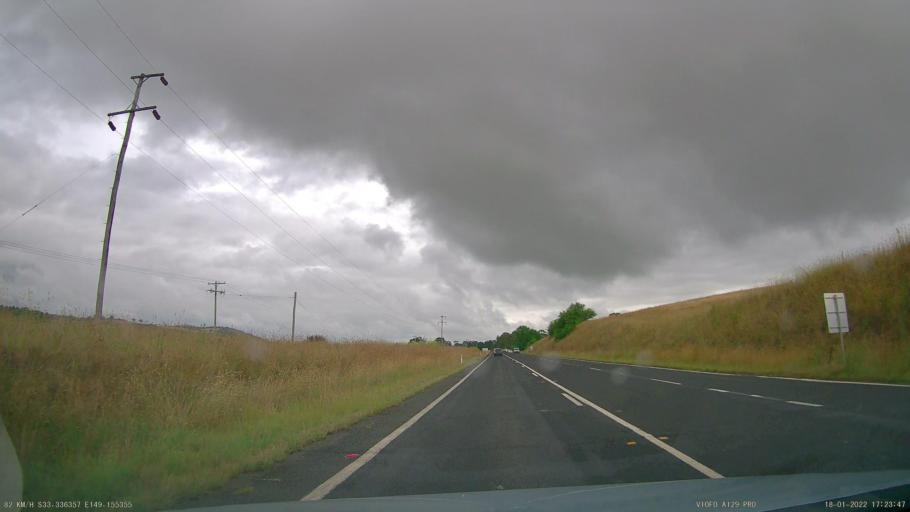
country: AU
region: New South Wales
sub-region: Orange Municipality
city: Orange
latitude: -33.3364
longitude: 149.1554
